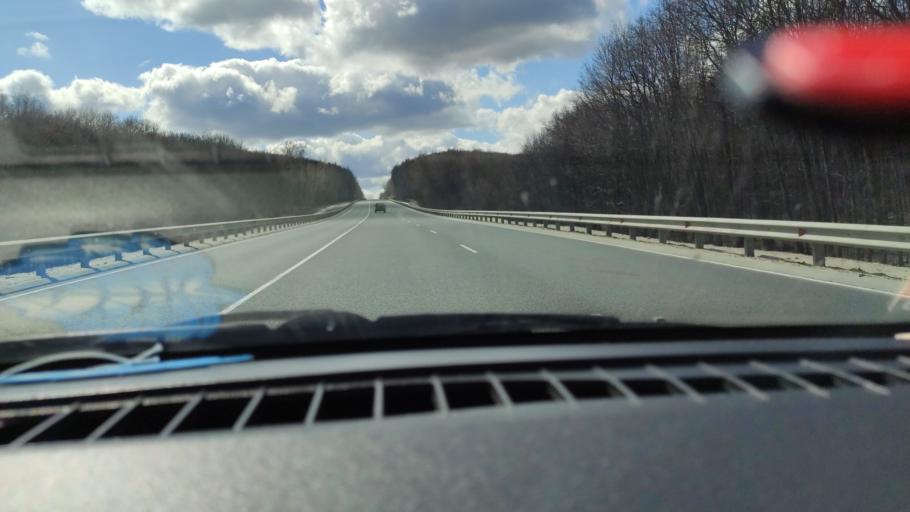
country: RU
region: Saratov
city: Khvalynsk
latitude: 52.5032
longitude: 48.0149
